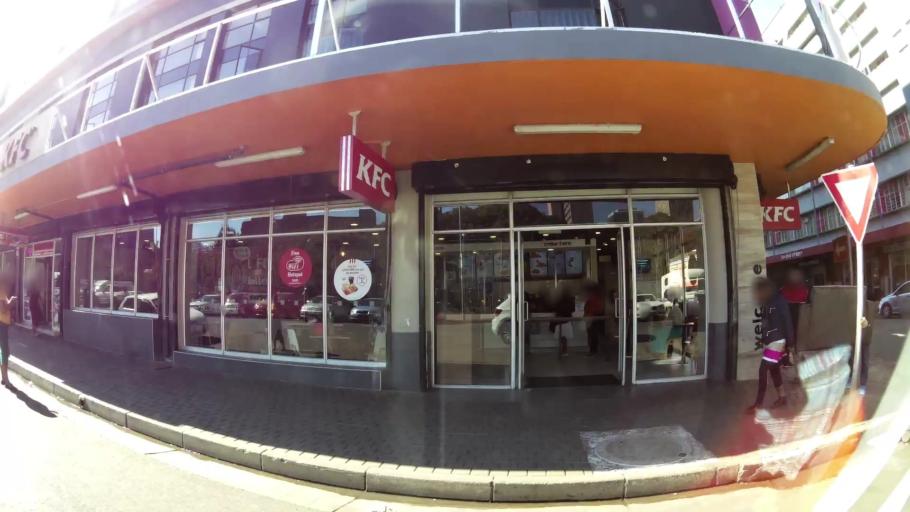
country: ZA
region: Gauteng
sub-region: City of Johannesburg Metropolitan Municipality
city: Johannesburg
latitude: -26.1991
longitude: 28.0531
